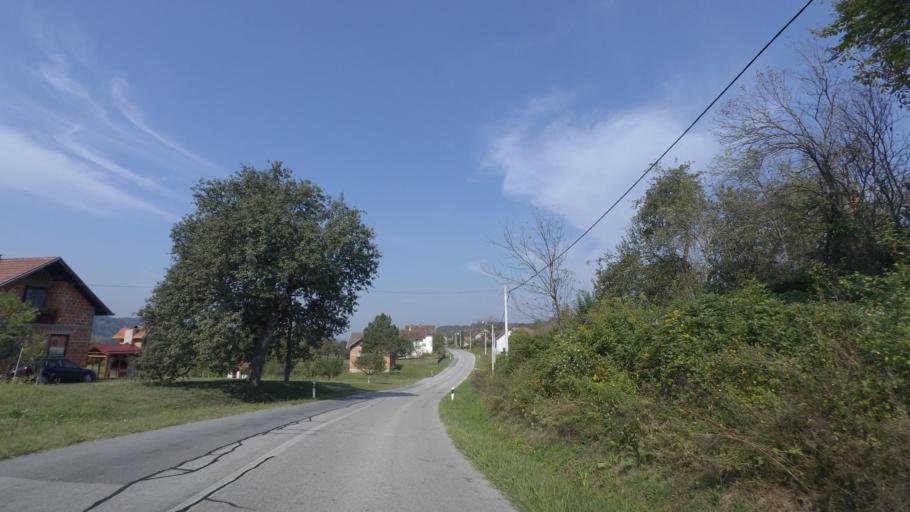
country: BA
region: Republika Srpska
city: Knezica
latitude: 45.2088
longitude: 16.6731
